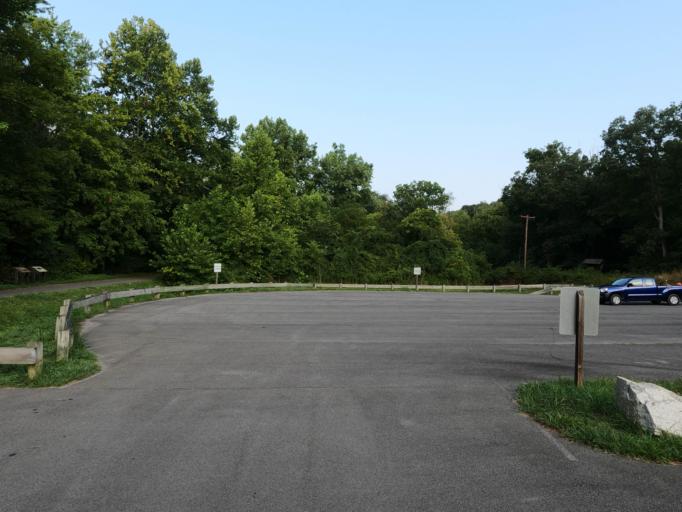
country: US
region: West Virginia
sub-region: Morgan County
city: Berkeley Springs
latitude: 39.6366
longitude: -78.3235
